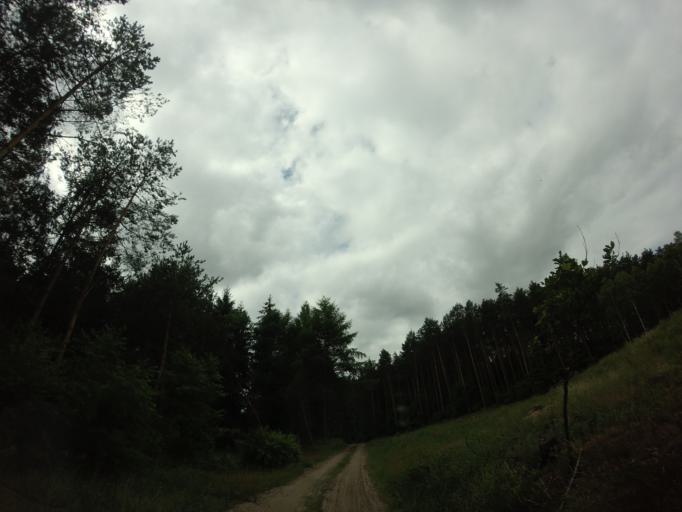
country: PL
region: West Pomeranian Voivodeship
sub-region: Powiat choszczenski
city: Bierzwnik
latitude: 52.9560
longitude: 15.6092
